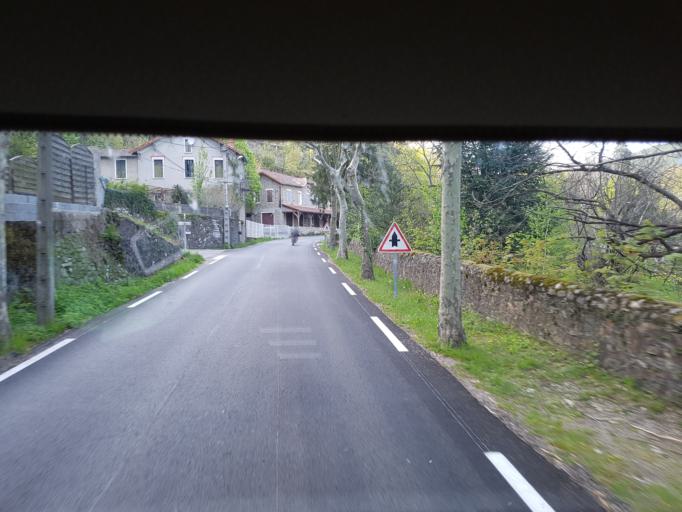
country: FR
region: Languedoc-Roussillon
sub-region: Departement du Gard
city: Branoux-les-Taillades
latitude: 44.3471
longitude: 3.9490
